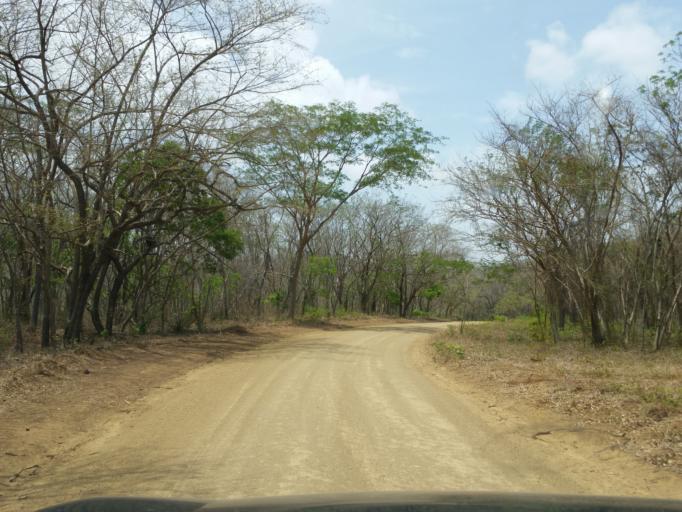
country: NI
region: Rivas
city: Tola
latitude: 11.4324
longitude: -86.0767
